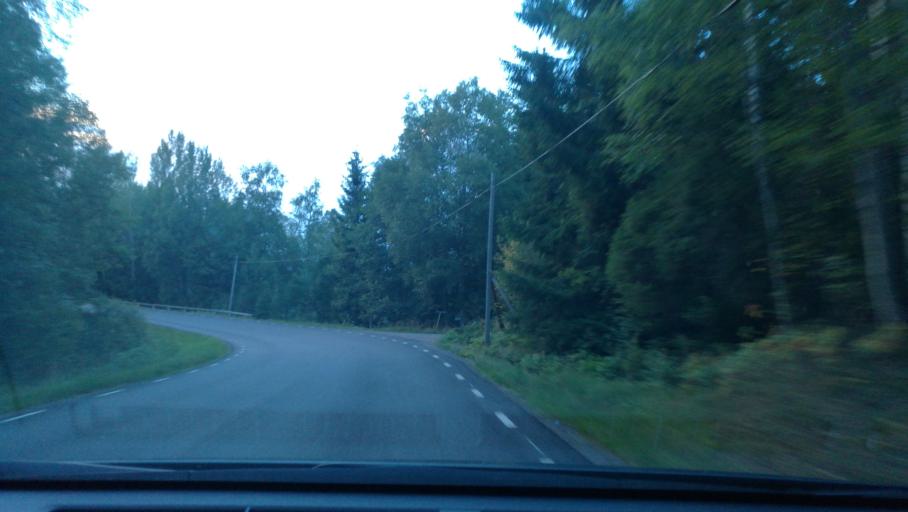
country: SE
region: OEstergoetland
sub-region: Norrkopings Kommun
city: Jursla
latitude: 58.8105
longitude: 16.0979
